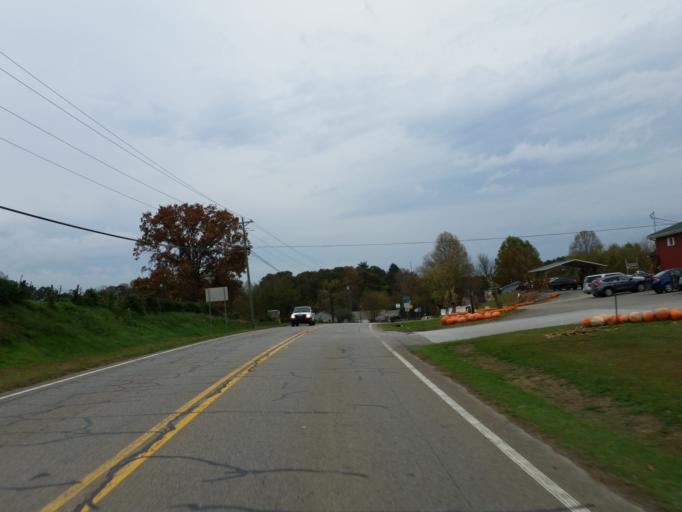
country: US
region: Georgia
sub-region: Gilmer County
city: Ellijay
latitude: 34.6235
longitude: -84.3803
